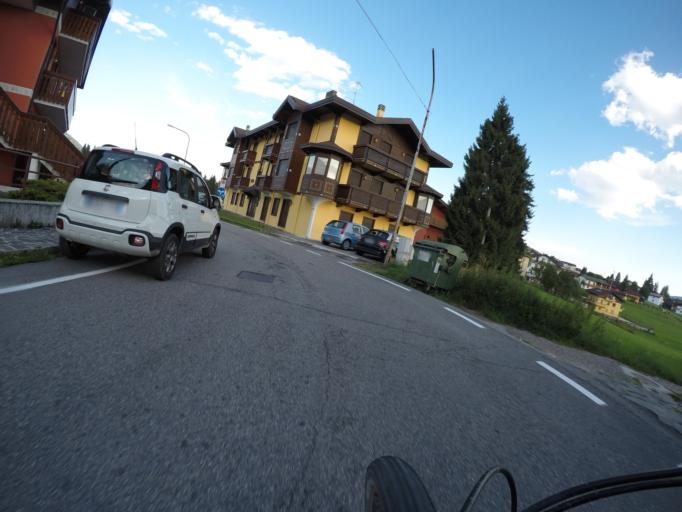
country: IT
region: Veneto
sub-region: Provincia di Vicenza
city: Gallio
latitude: 45.8900
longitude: 11.5471
